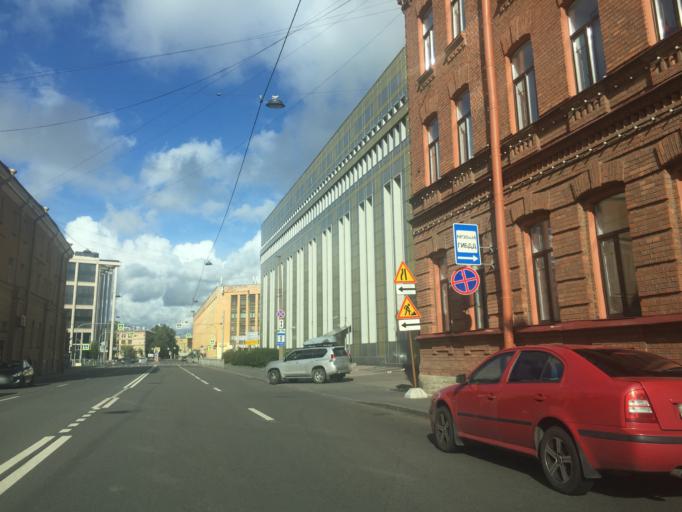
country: RU
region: St.-Petersburg
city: Centralniy
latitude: 59.9364
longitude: 30.3862
